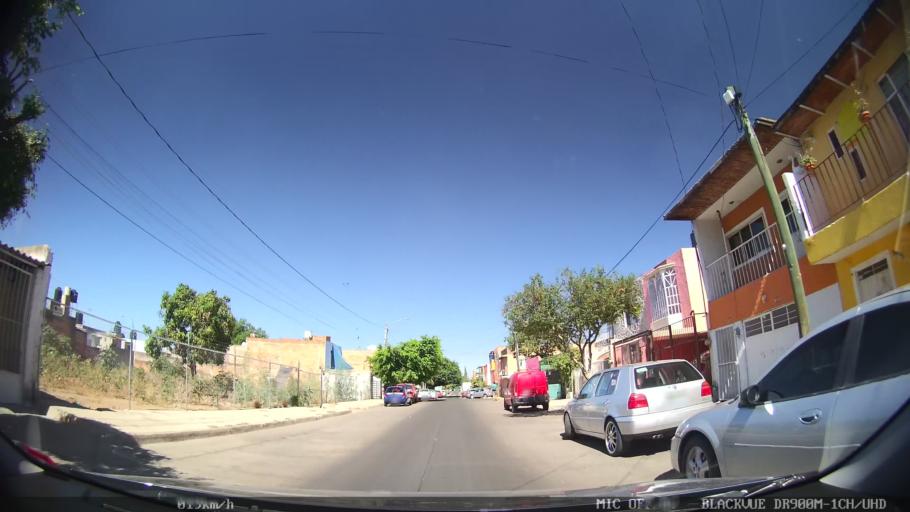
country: MX
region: Jalisco
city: Tlaquepaque
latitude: 20.6563
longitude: -103.2866
